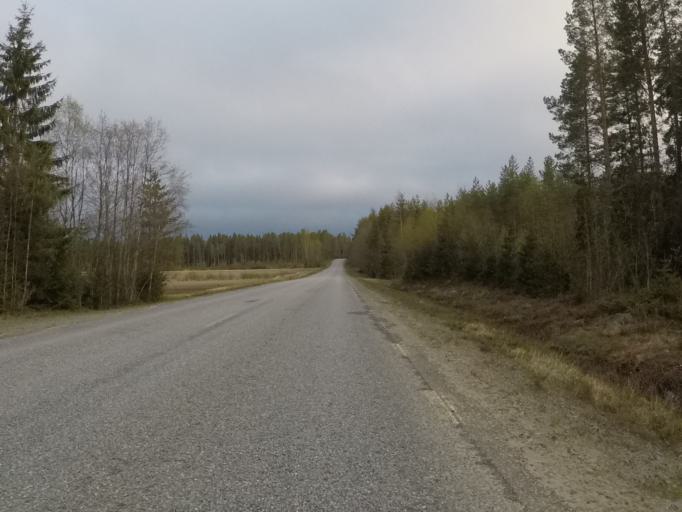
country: SE
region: Vaesterbotten
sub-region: Umea Kommun
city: Saevar
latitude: 63.9430
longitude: 20.7885
